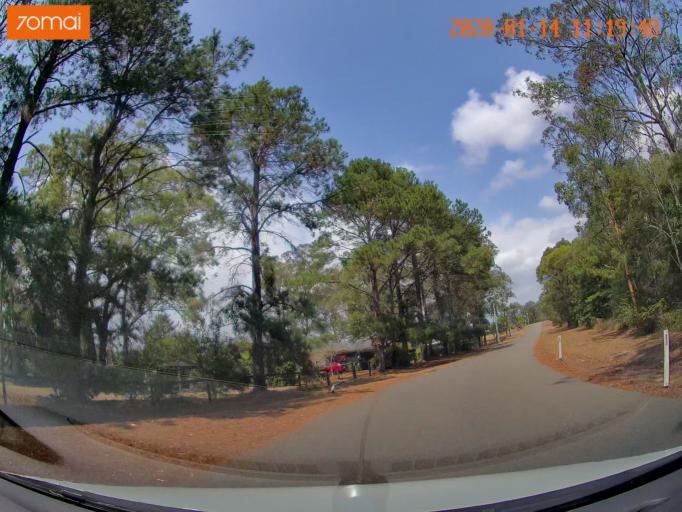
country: AU
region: New South Wales
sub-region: Lake Macquarie Shire
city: Cooranbong
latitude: -33.0998
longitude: 151.4599
